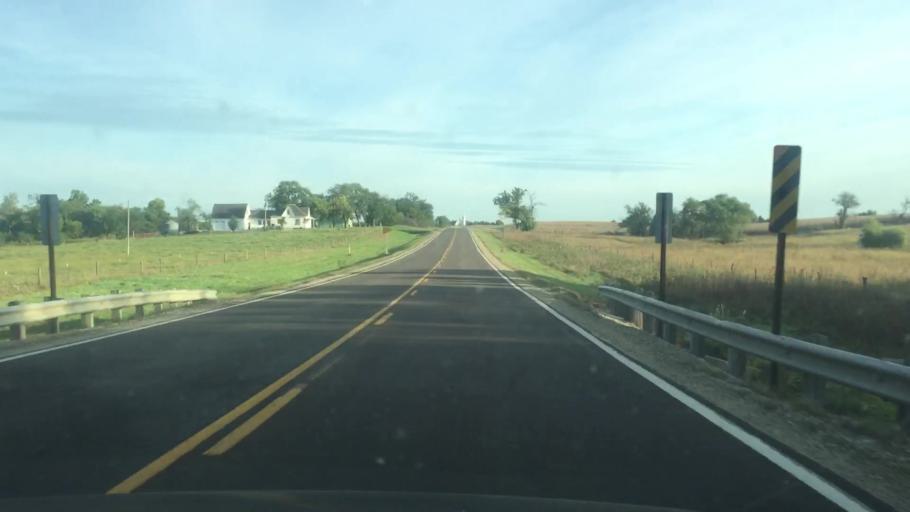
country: US
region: Nebraska
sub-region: Gage County
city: Wymore
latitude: 39.9922
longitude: -96.6574
